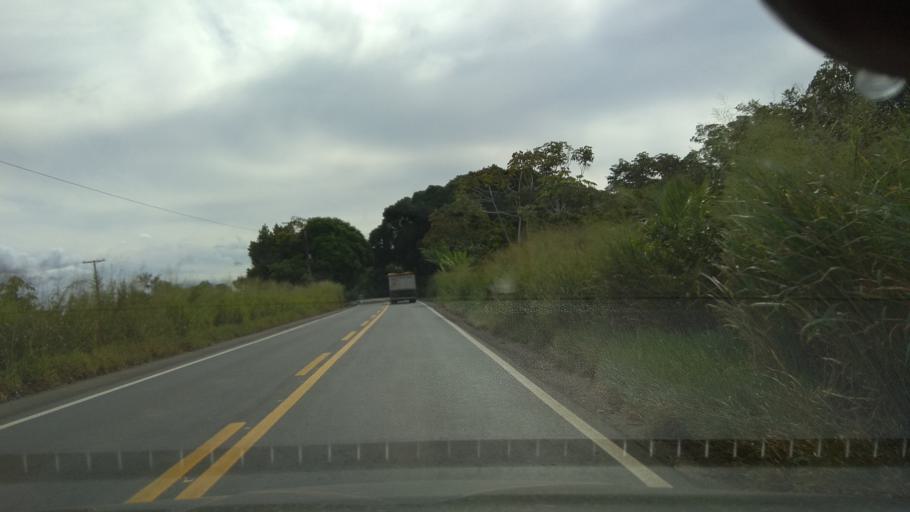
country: BR
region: Bahia
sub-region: Ubata
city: Ubata
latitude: -14.1989
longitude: -39.6107
